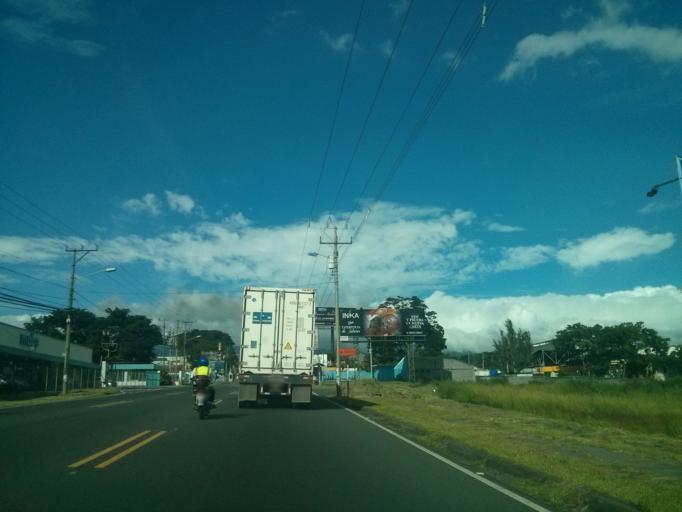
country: CR
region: Heredia
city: San Francisco
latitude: 9.9739
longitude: -84.1127
